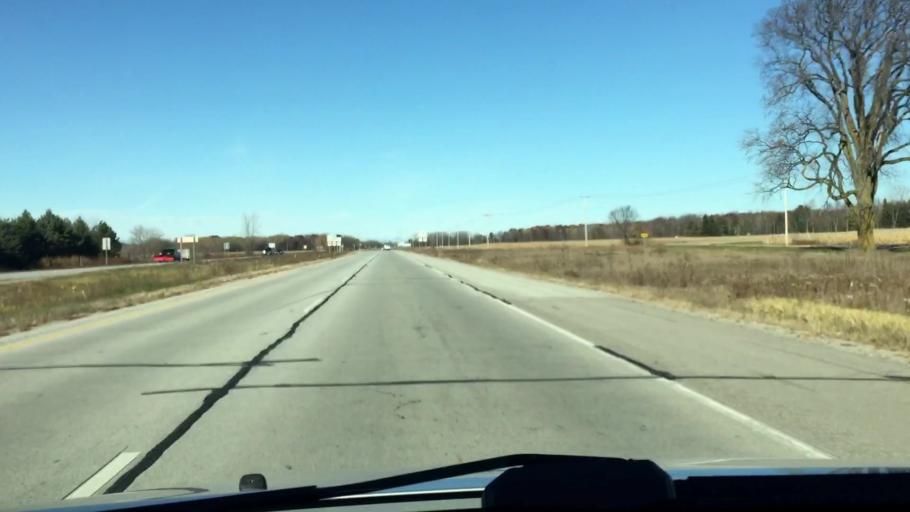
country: US
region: Wisconsin
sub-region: Brown County
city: Oneida
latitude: 44.5753
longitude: -88.1678
